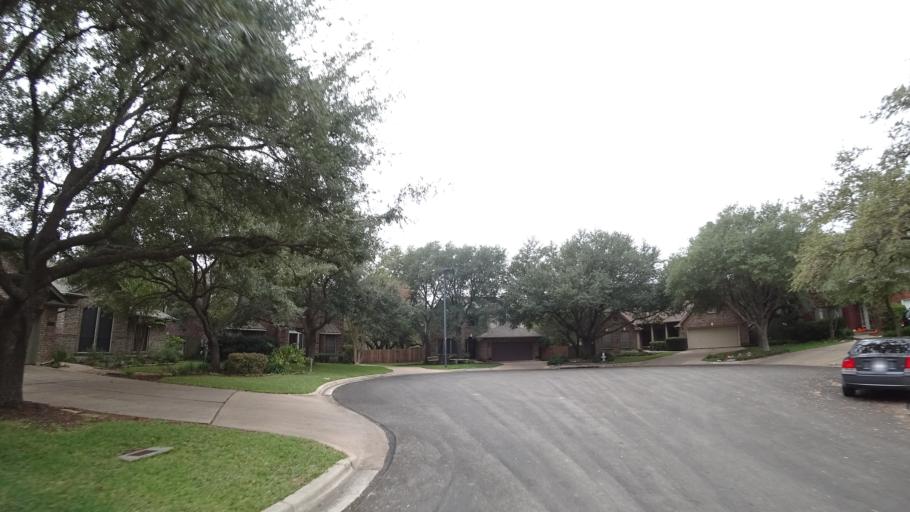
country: US
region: Texas
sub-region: Travis County
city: Shady Hollow
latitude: 30.1858
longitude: -97.8936
